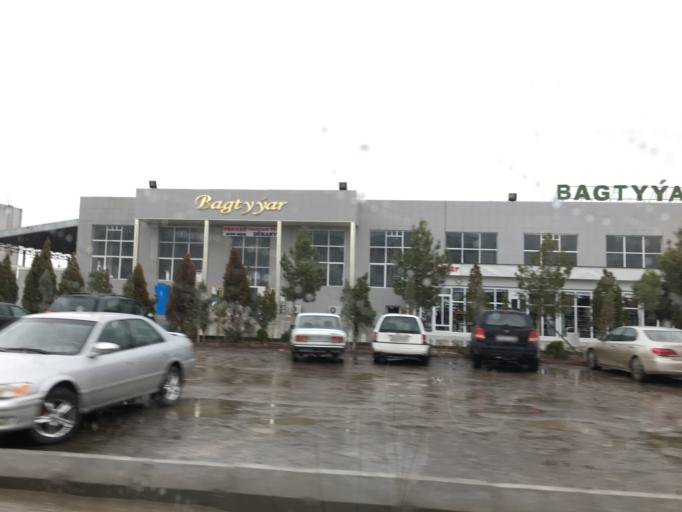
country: TM
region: Mary
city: Mary
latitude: 37.5757
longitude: 61.8341
